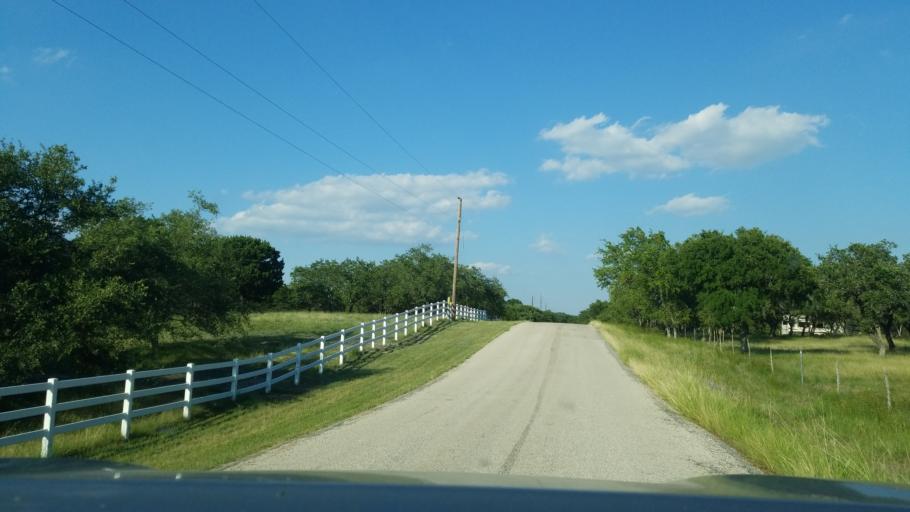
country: US
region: Texas
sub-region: Comal County
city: Bulverde
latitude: 29.7796
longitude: -98.4446
